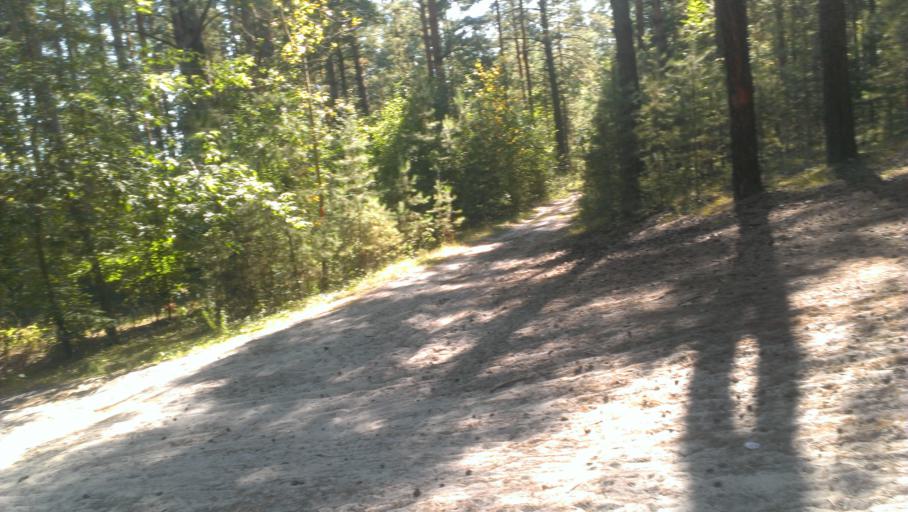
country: RU
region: Altai Krai
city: Yuzhnyy
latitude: 53.3158
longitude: 83.6888
